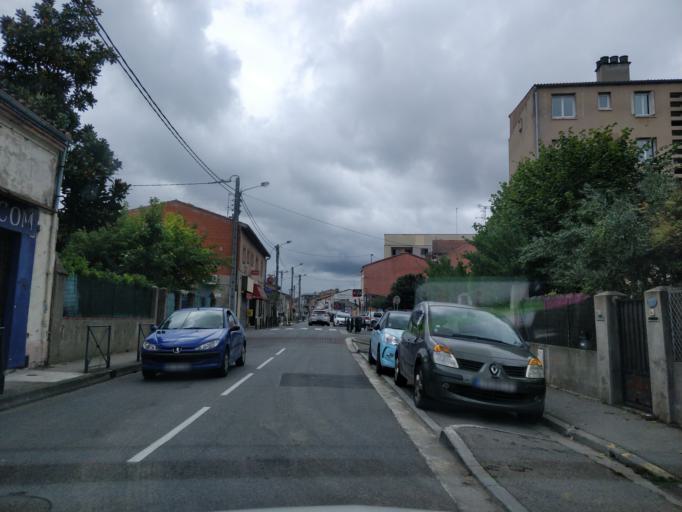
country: FR
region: Midi-Pyrenees
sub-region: Departement de la Haute-Garonne
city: Toulouse
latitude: 43.5853
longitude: 1.4165
